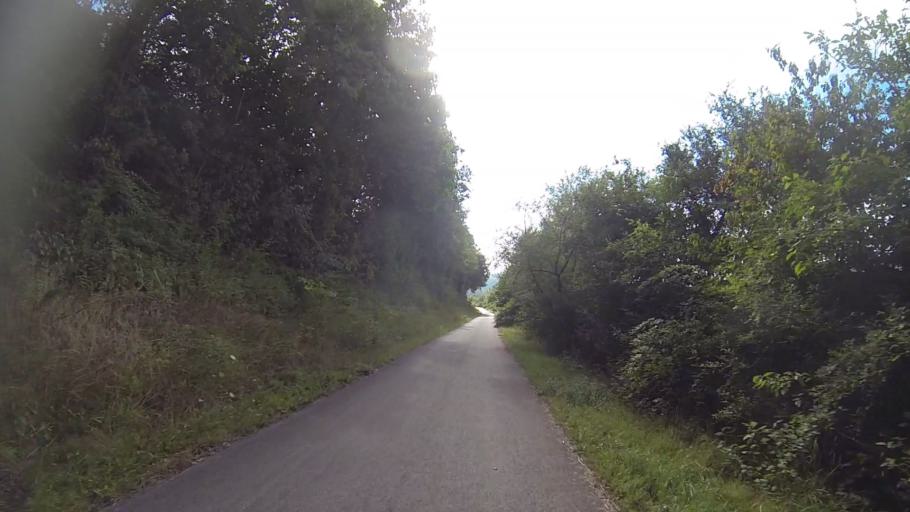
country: DE
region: Rheinland-Pfalz
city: Kenn
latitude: 49.8014
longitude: 6.6971
